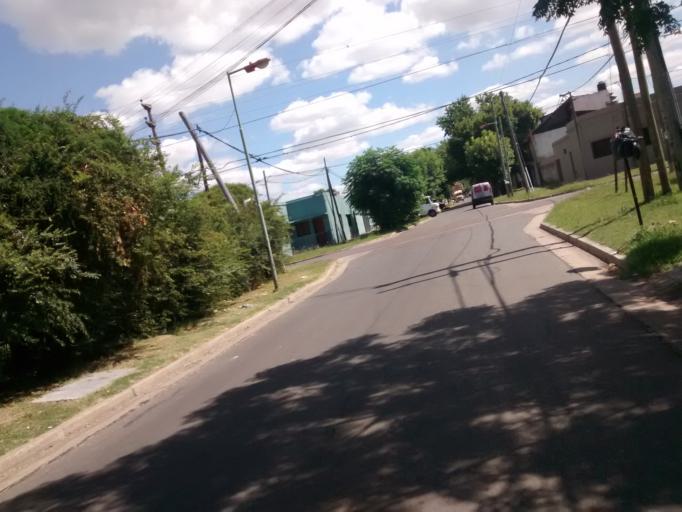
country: AR
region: Buenos Aires
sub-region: Partido de La Plata
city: La Plata
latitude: -34.9447
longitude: -57.9740
